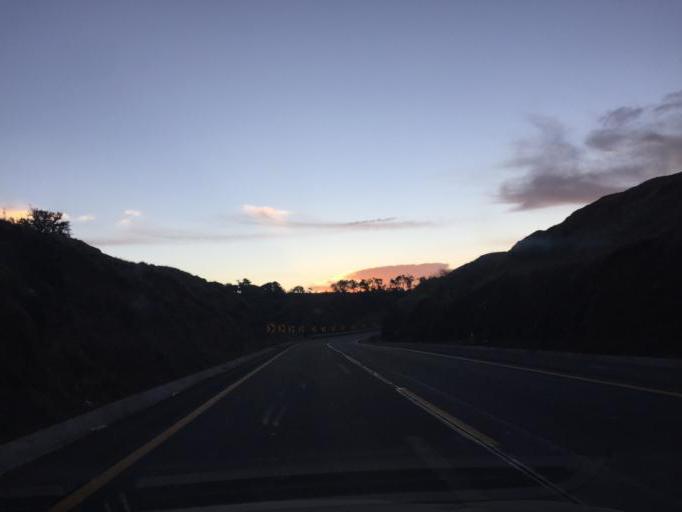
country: MX
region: Puebla
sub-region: Esperanza
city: San Jose Cuyachapa
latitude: 18.8312
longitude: -97.3262
